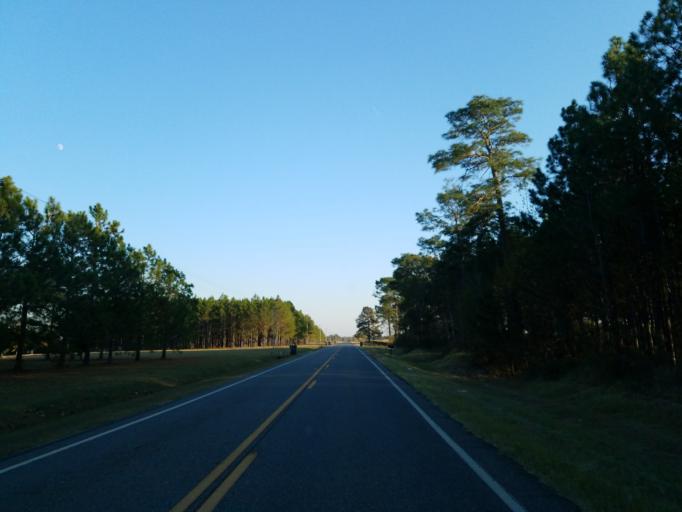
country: US
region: Georgia
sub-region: Turner County
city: Ashburn
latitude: 31.8659
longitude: -83.6535
